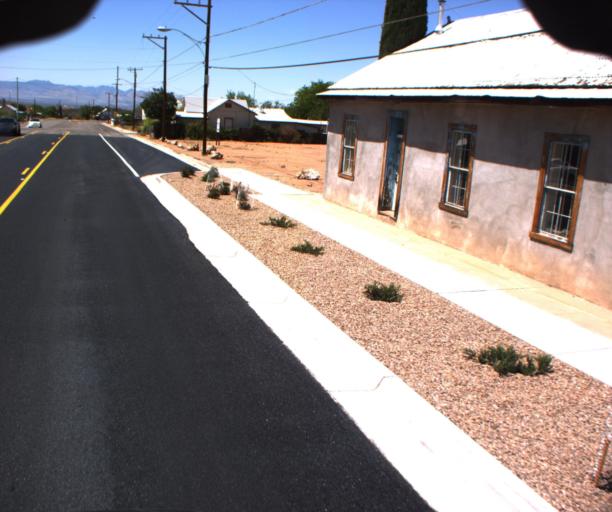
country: US
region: Arizona
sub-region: Cochise County
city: Tombstone
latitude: 31.7142
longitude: -110.0679
